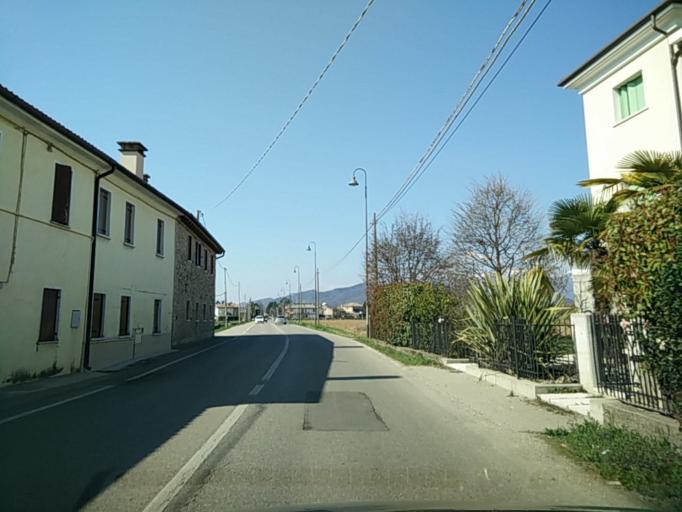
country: IT
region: Veneto
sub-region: Provincia di Treviso
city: Ciano
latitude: 45.8258
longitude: 12.0430
